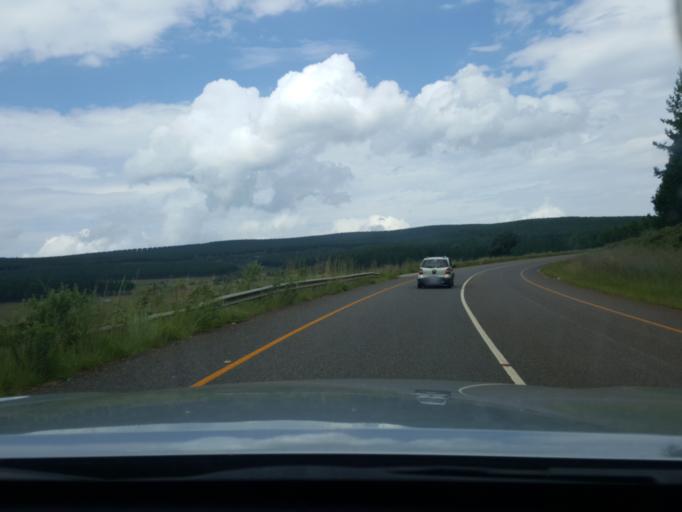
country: ZA
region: Mpumalanga
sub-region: Ehlanzeni District
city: Graksop
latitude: -25.1312
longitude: 30.8166
